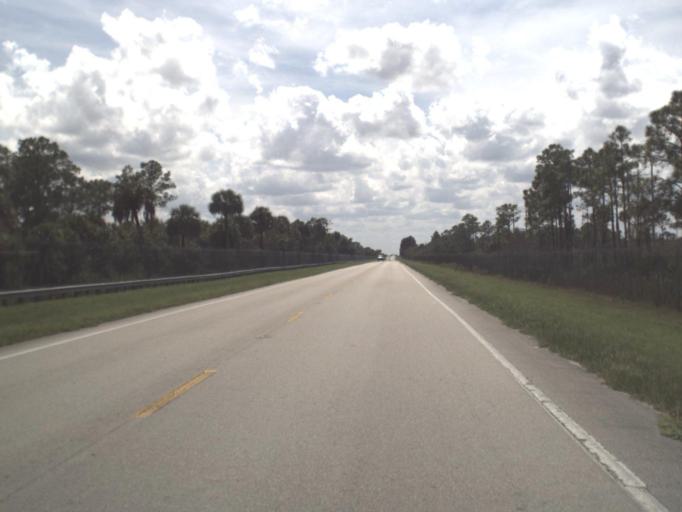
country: US
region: Florida
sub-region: Collier County
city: Immokalee
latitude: 26.1799
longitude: -81.3457
